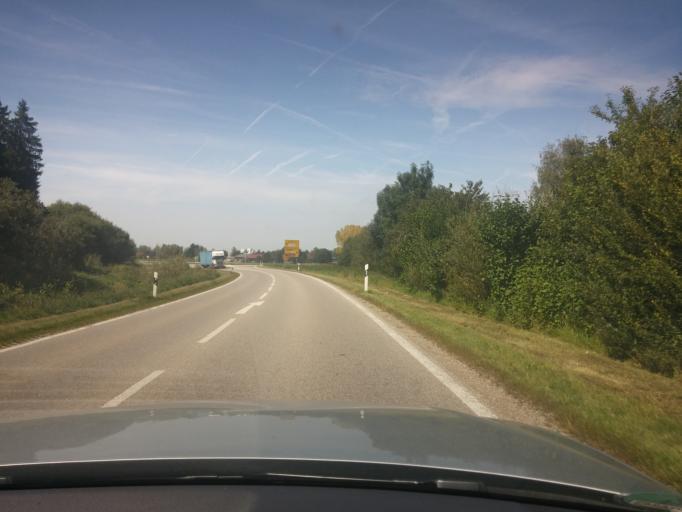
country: DE
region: Baden-Wuerttemberg
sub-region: Tuebingen Region
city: Bad Buchau
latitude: 48.0501
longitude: 9.6232
